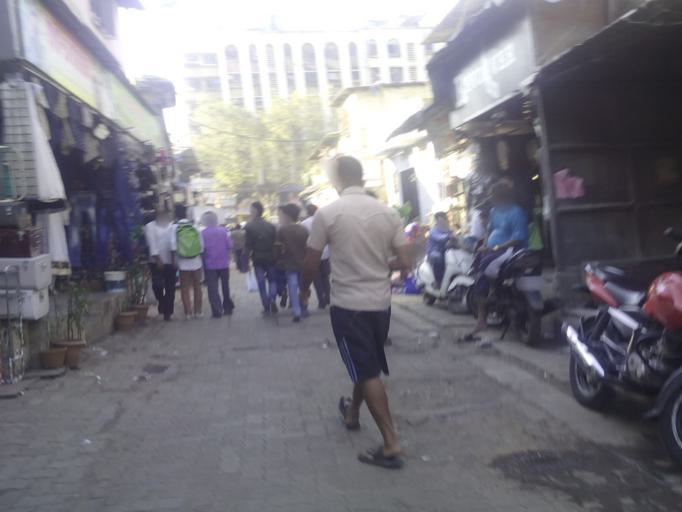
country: IN
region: Maharashtra
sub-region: Mumbai Suburban
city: Mumbai
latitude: 19.0417
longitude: 72.8570
